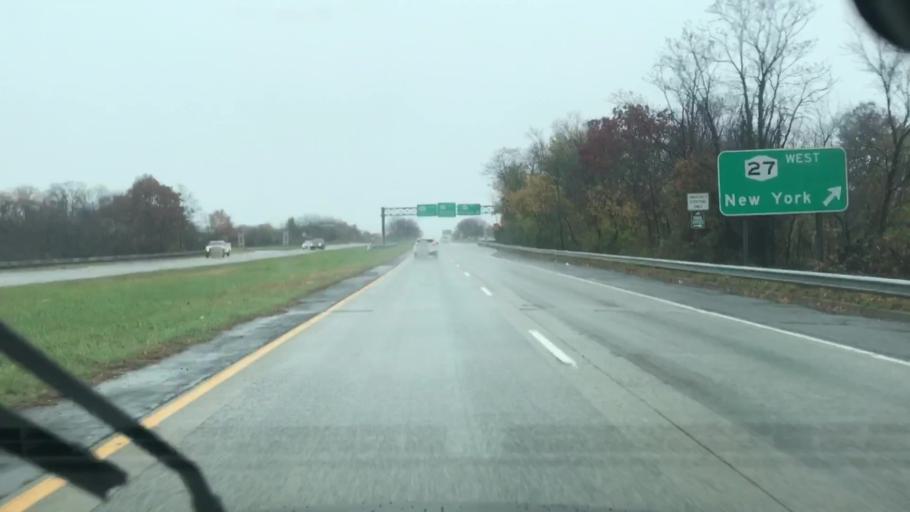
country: US
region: New York
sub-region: Suffolk County
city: North Babylon
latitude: 40.7209
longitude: -73.3145
